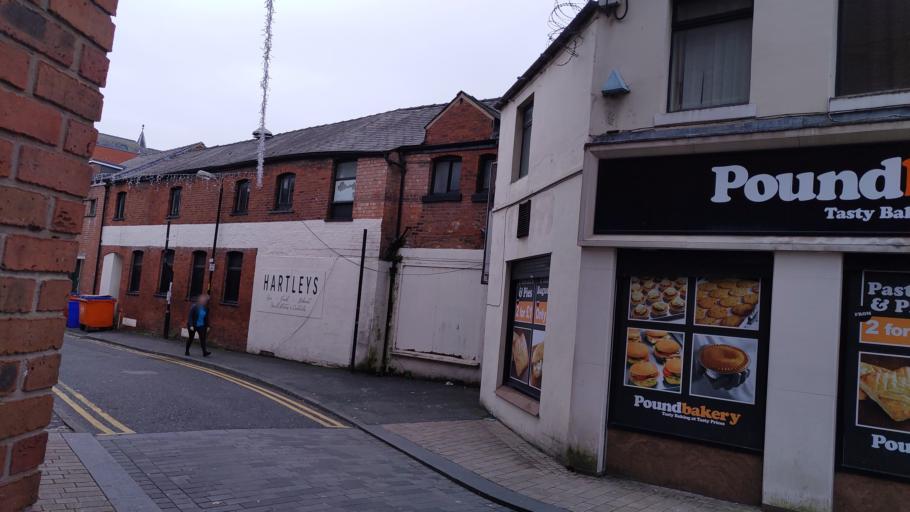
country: GB
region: England
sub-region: Lancashire
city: Preston
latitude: 53.7578
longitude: -2.7038
